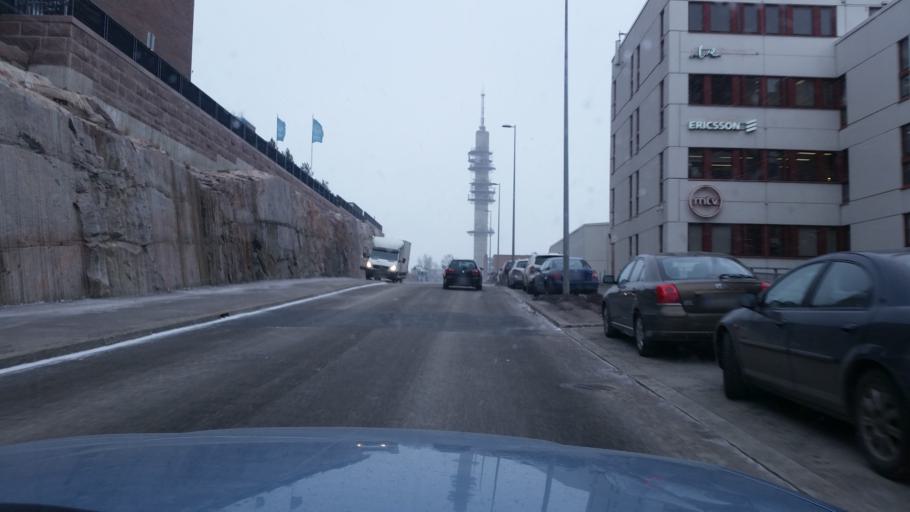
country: FI
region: Uusimaa
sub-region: Helsinki
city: Helsinki
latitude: 60.2067
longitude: 24.9158
